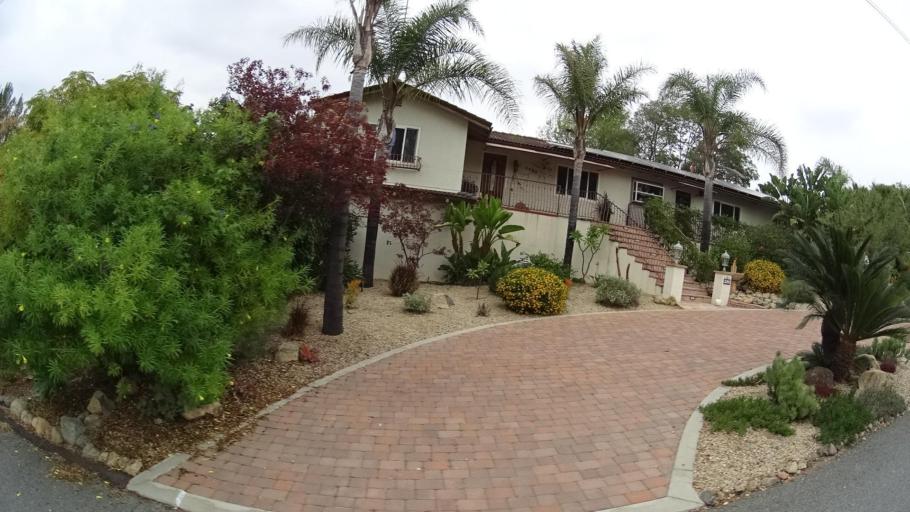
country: US
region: California
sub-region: San Diego County
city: Casa de Oro-Mount Helix
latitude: 32.7592
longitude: -116.9726
